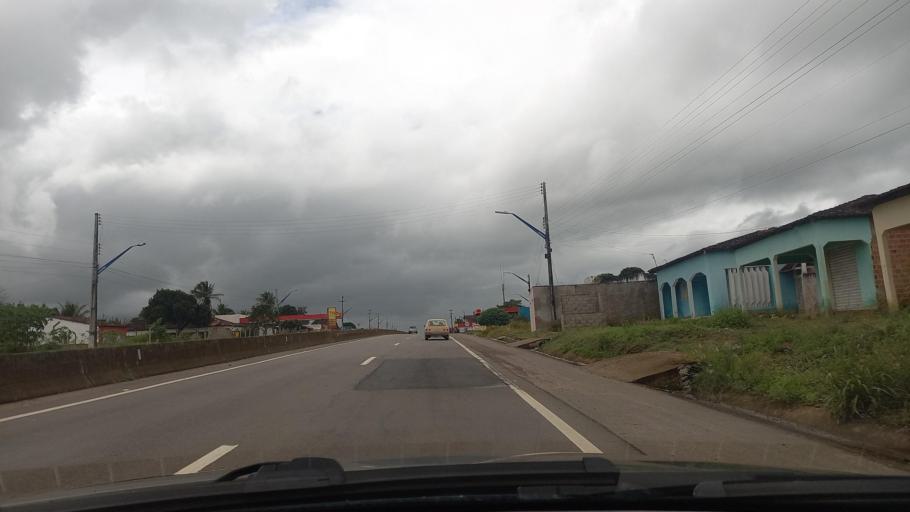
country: BR
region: Alagoas
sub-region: Limoeiro De Anadia
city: Limoeiro de Anadia
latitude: -9.7424
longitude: -36.4724
